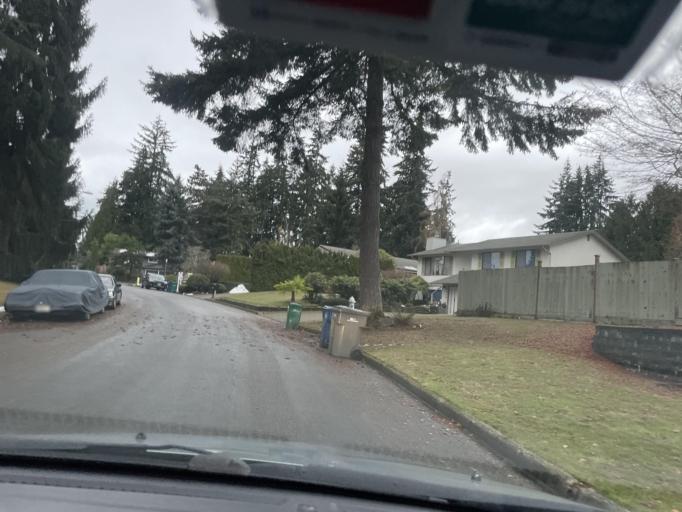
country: US
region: Washington
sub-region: King County
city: Kingsgate
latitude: 47.7243
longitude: -122.1792
